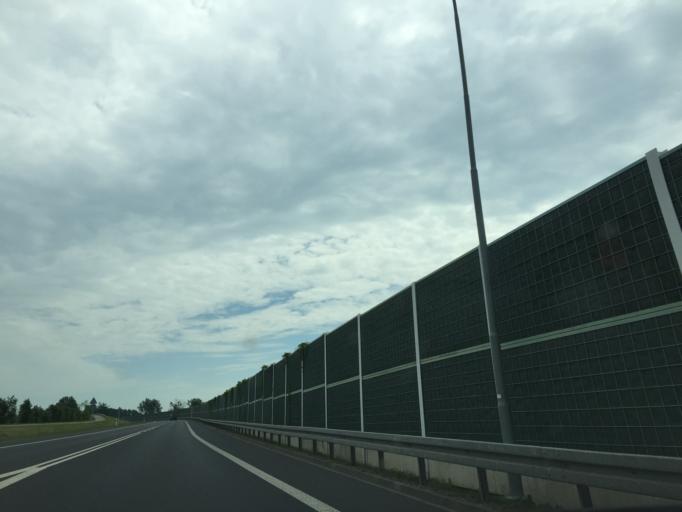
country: PL
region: Warmian-Masurian Voivodeship
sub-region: Powiat mragowski
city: Mragowo
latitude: 53.8811
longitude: 21.3365
